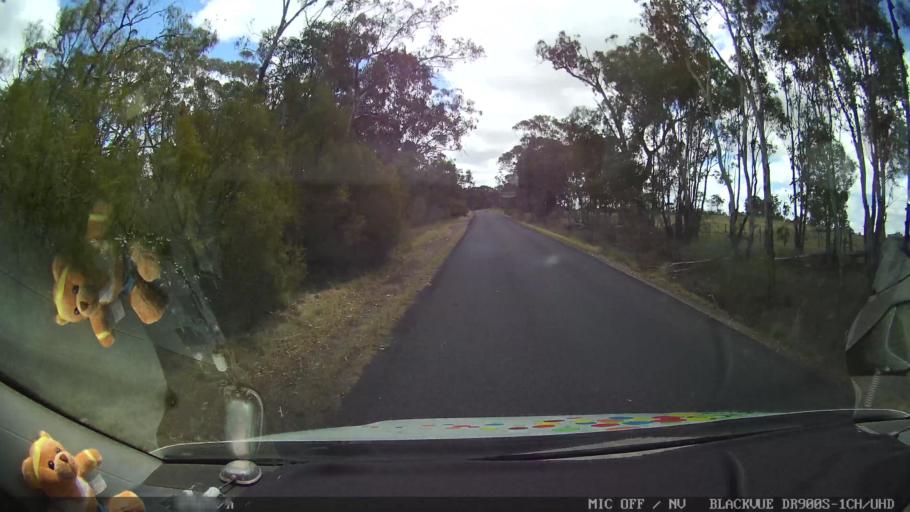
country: AU
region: New South Wales
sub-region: Glen Innes Severn
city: Glen Innes
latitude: -29.4323
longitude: 151.7870
